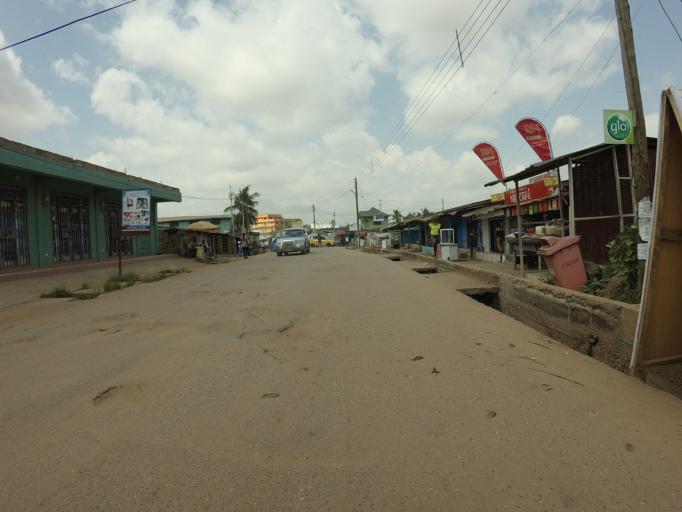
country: GH
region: Greater Accra
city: Dome
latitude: 5.6124
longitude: -0.2450
